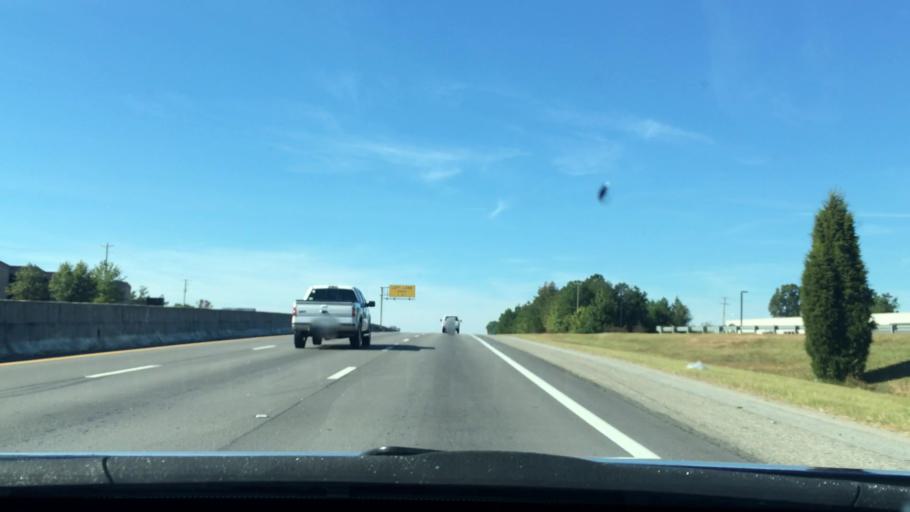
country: US
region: South Carolina
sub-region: Lexington County
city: Irmo
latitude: 34.0922
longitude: -81.1671
